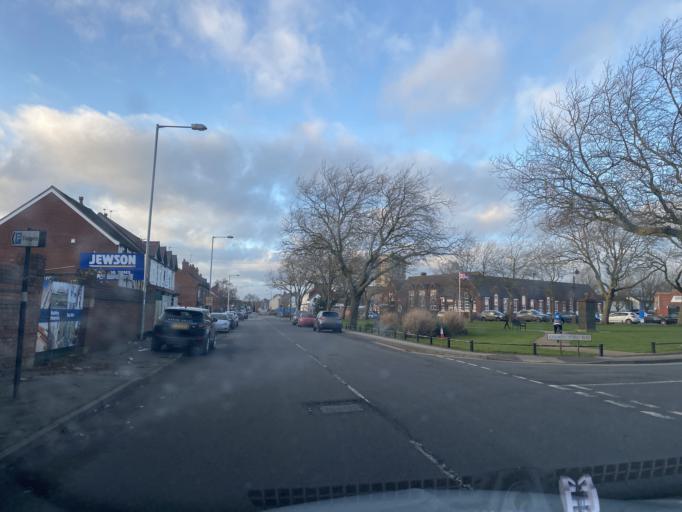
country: GB
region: England
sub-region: Walsall
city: Bloxwich
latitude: 52.6154
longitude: -2.0064
